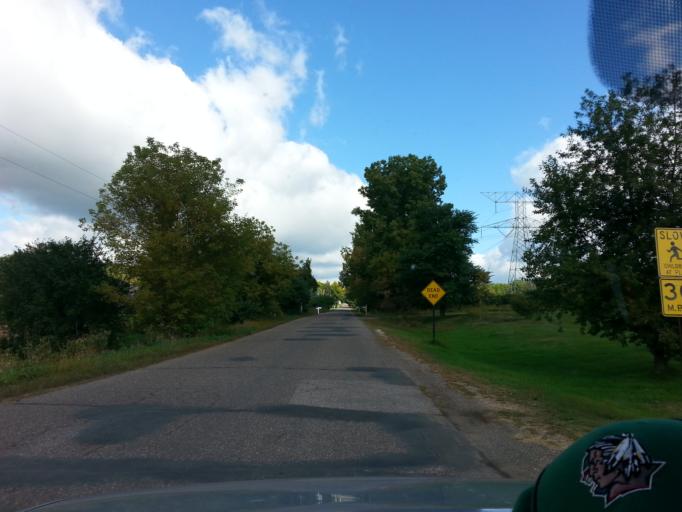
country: US
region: Minnesota
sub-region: Washington County
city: Lakeland
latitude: 44.9636
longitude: -92.8124
